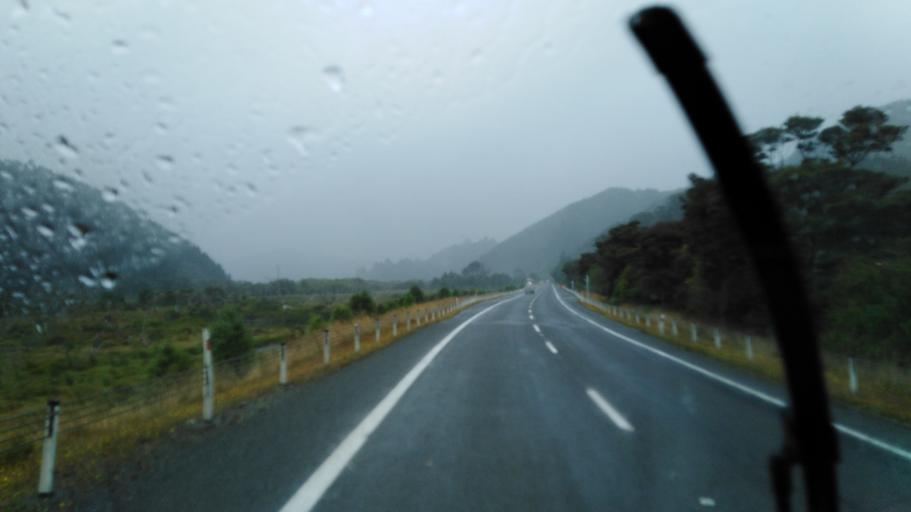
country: NZ
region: Marlborough
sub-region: Marlborough District
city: Blenheim
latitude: -41.3946
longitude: 173.9510
